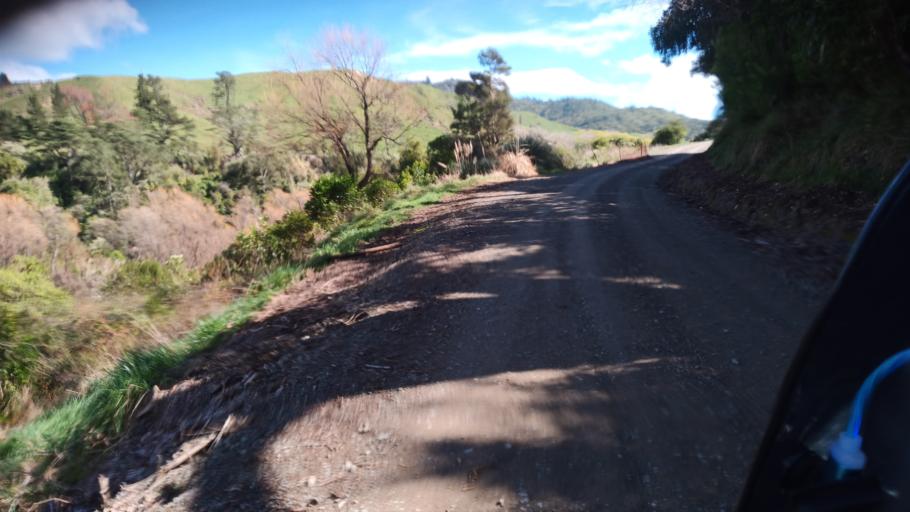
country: NZ
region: Hawke's Bay
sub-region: Wairoa District
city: Wairoa
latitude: -38.8374
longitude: 177.1643
